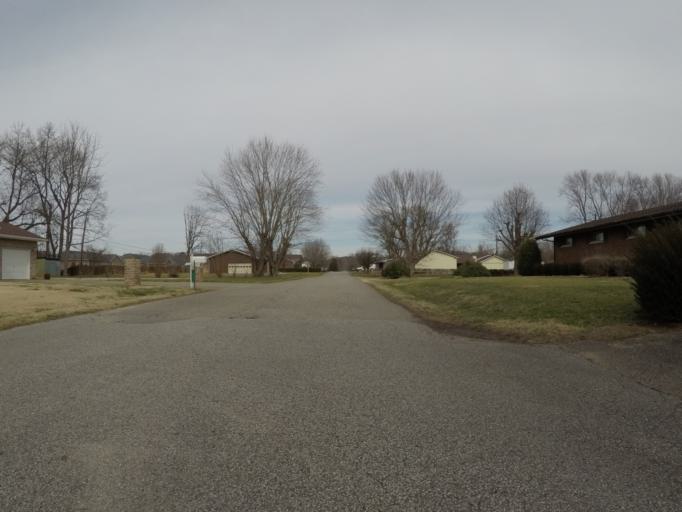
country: US
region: West Virginia
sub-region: Cabell County
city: Pea Ridge
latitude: 38.4430
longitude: -82.3477
